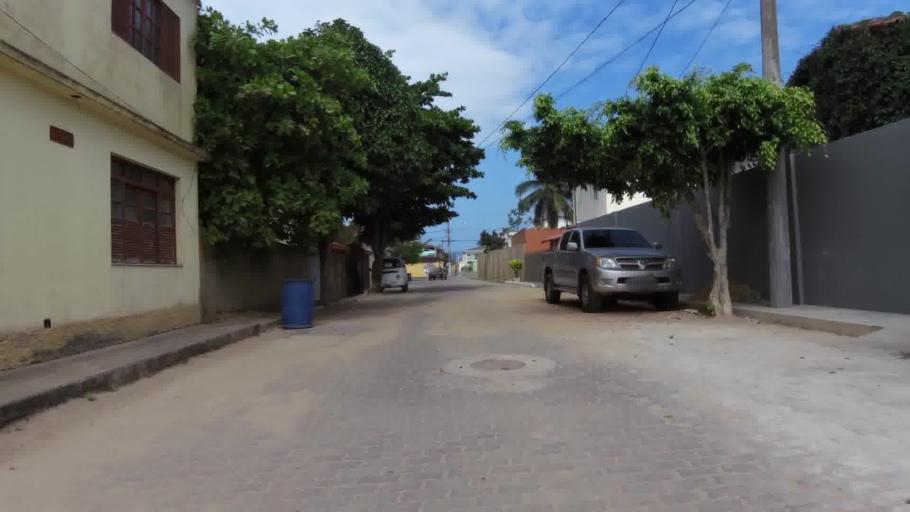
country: BR
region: Espirito Santo
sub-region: Marataizes
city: Marataizes
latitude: -21.0267
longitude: -40.8153
